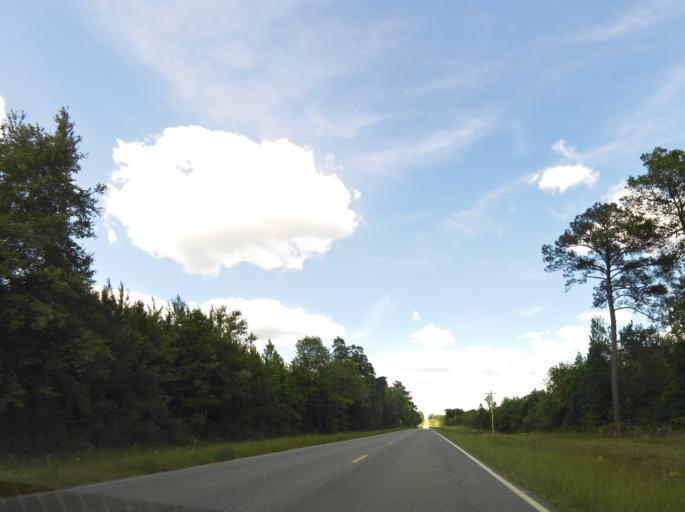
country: US
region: Georgia
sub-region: Telfair County
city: Helena
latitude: 32.2403
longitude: -82.9471
